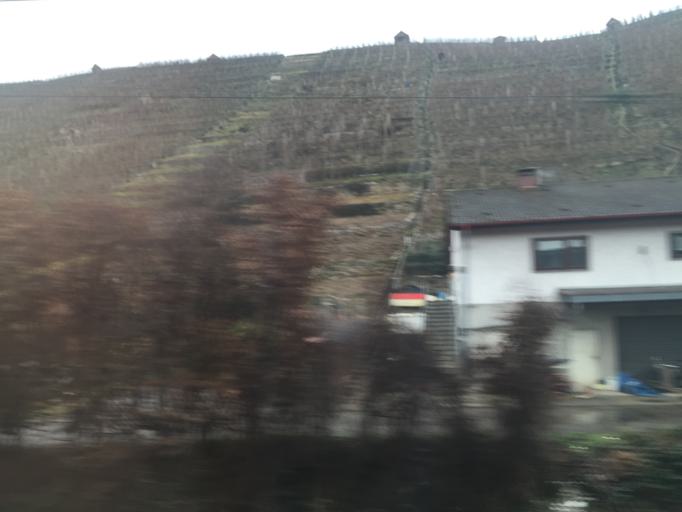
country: DE
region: Baden-Wuerttemberg
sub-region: Regierungsbezirk Stuttgart
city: Besigheim
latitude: 49.0014
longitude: 9.1347
